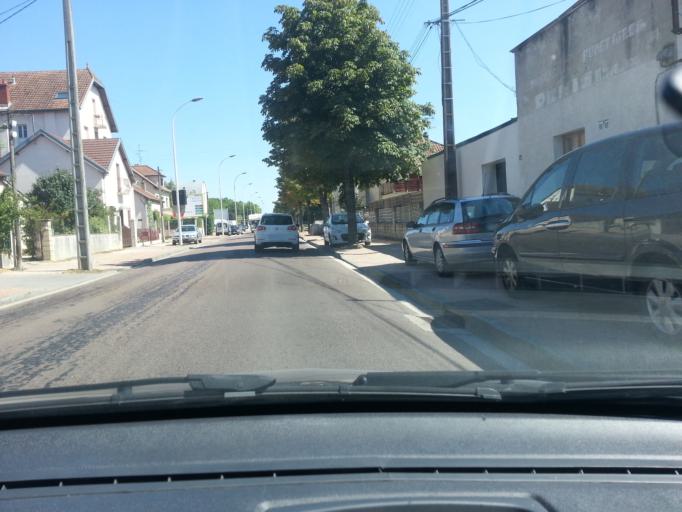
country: FR
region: Bourgogne
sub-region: Departement de la Cote-d'Or
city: Longvic
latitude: 47.3058
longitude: 5.0603
